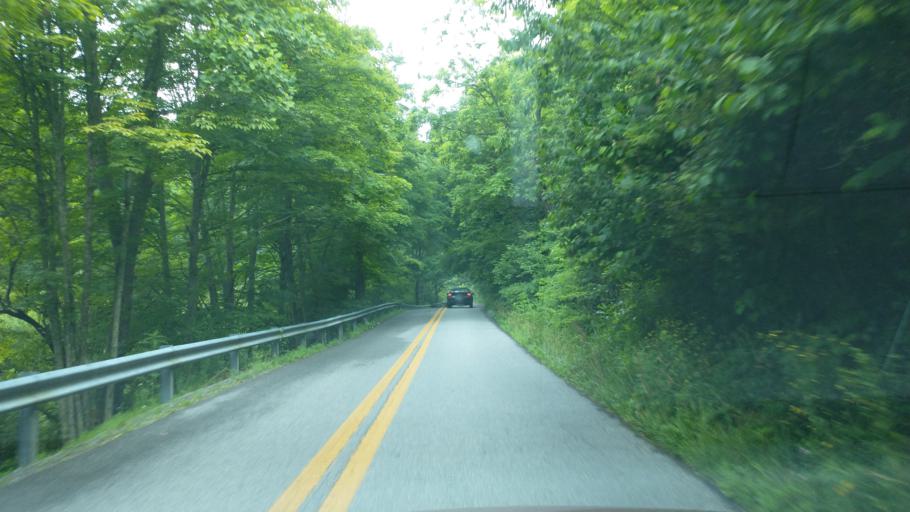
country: US
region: West Virginia
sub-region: Mercer County
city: Athens
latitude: 37.4281
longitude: -80.9869
